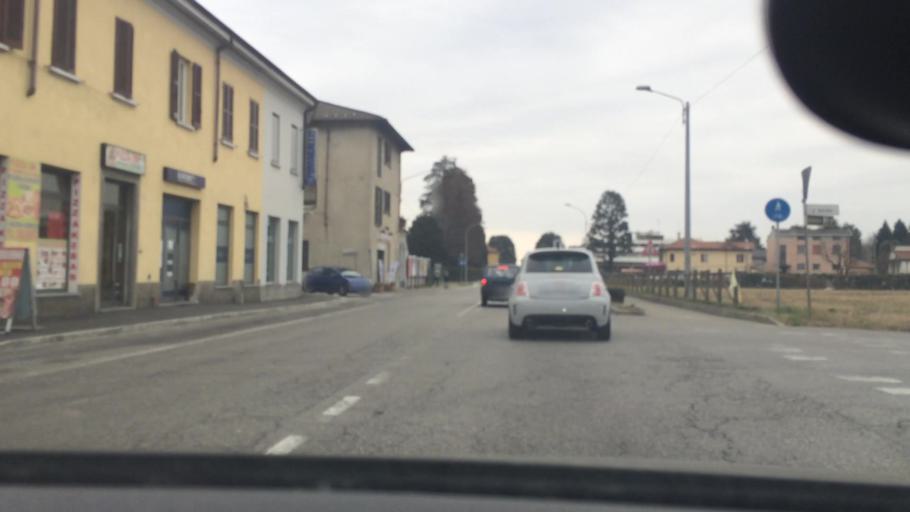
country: IT
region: Lombardy
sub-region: Provincia di Monza e Brianza
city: Lentate sul Seveso
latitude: 45.6790
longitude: 9.1143
